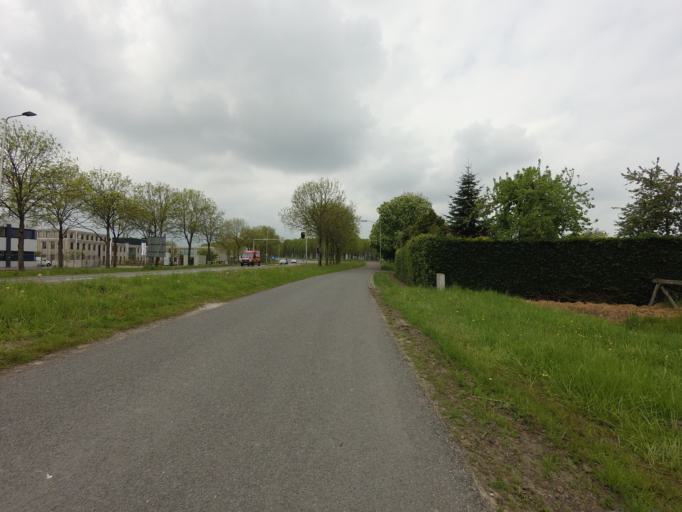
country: NL
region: Utrecht
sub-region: Gemeente Utrecht
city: Lunetten
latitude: 52.0428
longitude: 5.1462
